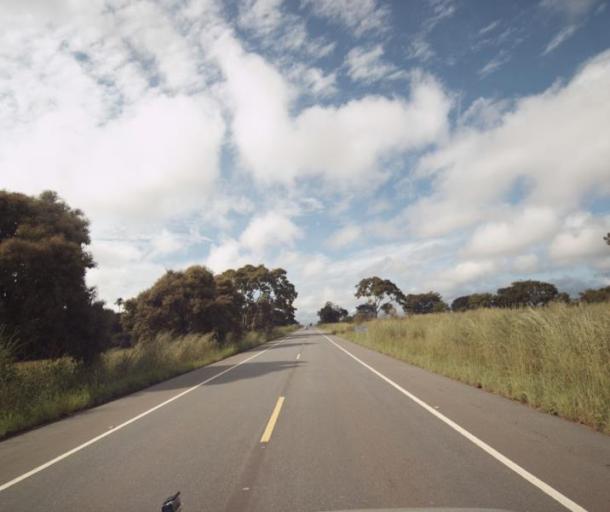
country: BR
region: Goias
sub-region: Barro Alto
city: Barro Alto
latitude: -15.2445
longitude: -48.6903
